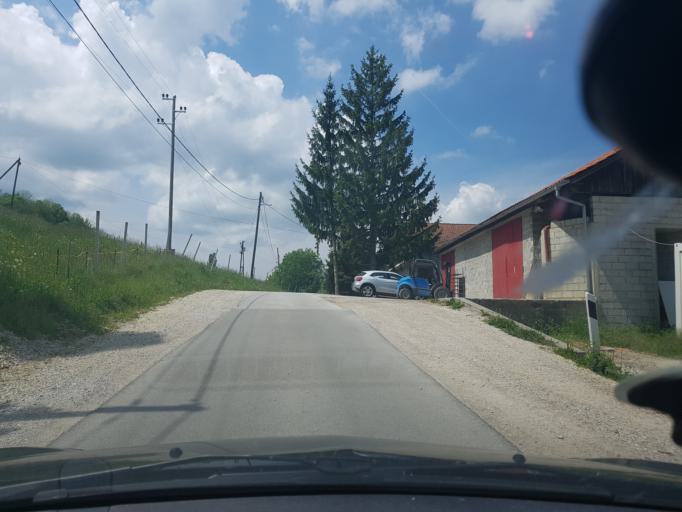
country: SI
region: Rogatec
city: Rogatec
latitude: 46.2124
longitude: 15.6958
